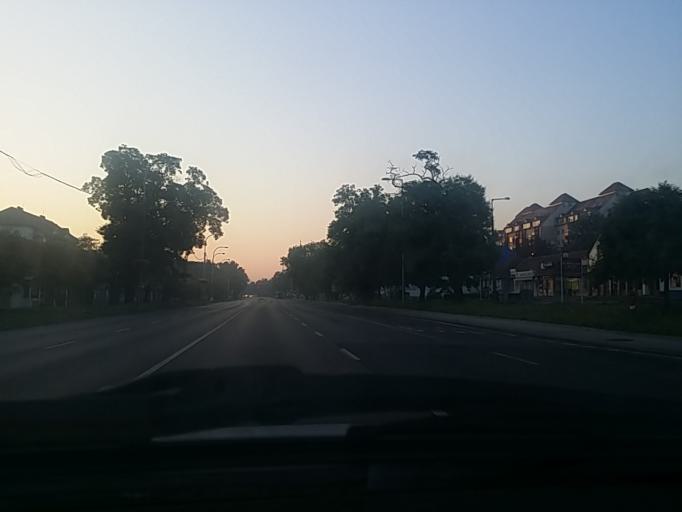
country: HU
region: Budapest
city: Budapest XVII. keruelet
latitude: 47.4831
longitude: 19.2393
